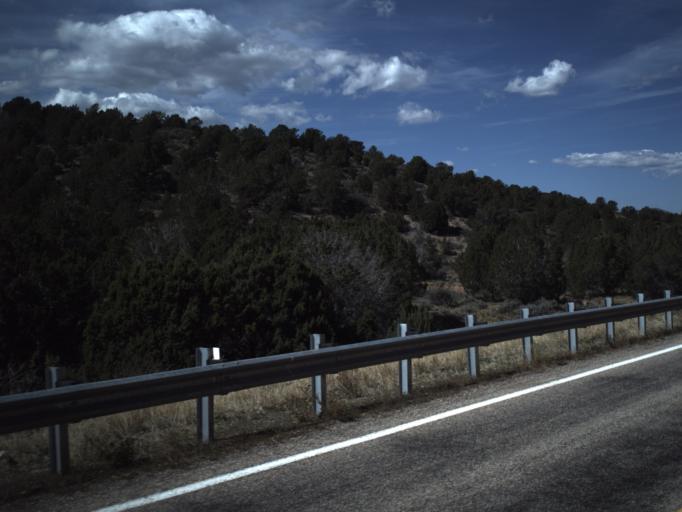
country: US
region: Utah
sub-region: Washington County
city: Enterprise
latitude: 37.5465
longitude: -113.6853
